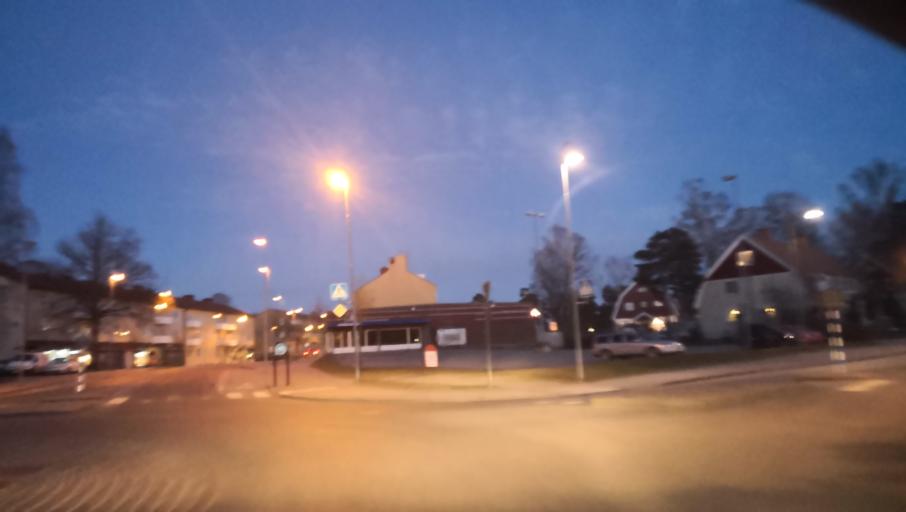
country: SE
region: Stockholm
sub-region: Nynashamns Kommun
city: Nynashamn
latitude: 58.9150
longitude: 17.9444
